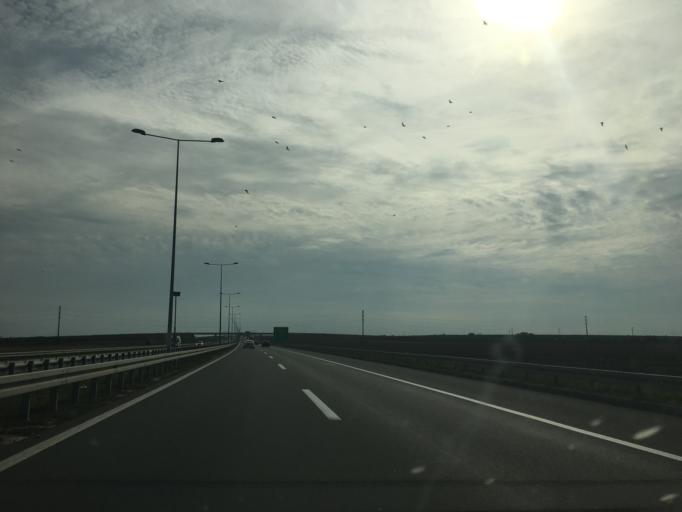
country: RS
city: Dobanovci
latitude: 44.8495
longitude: 20.2492
